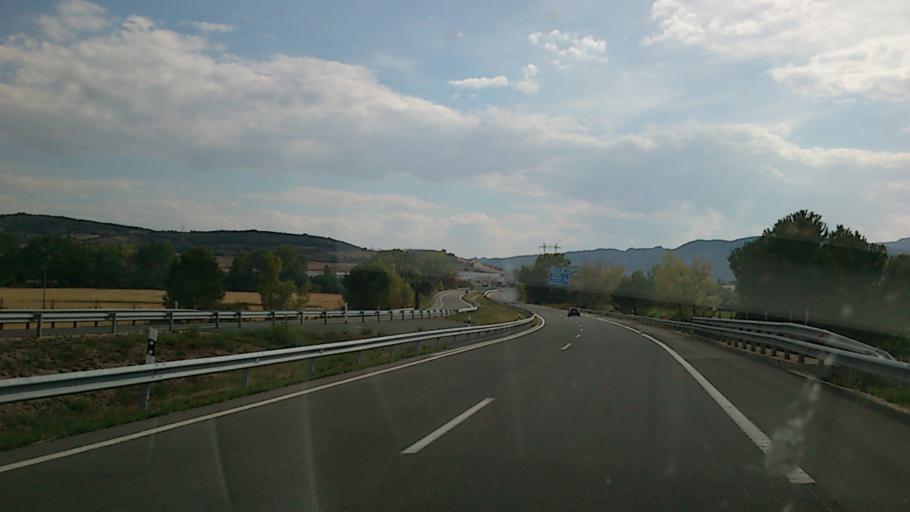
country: ES
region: Basque Country
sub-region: Provincia de Alava
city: Zambrana
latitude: 42.6864
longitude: -2.8919
